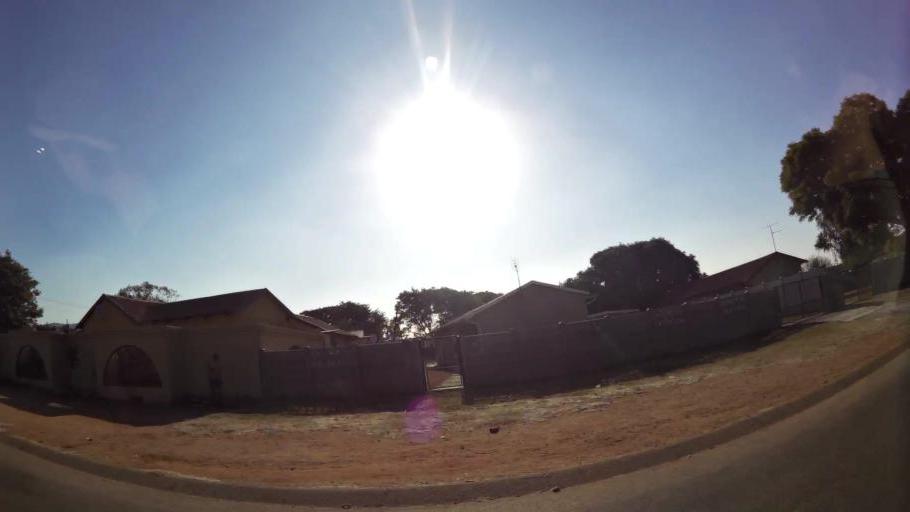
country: ZA
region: North-West
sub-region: Bojanala Platinum District Municipality
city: Rustenburg
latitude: -25.6488
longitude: 27.2293
